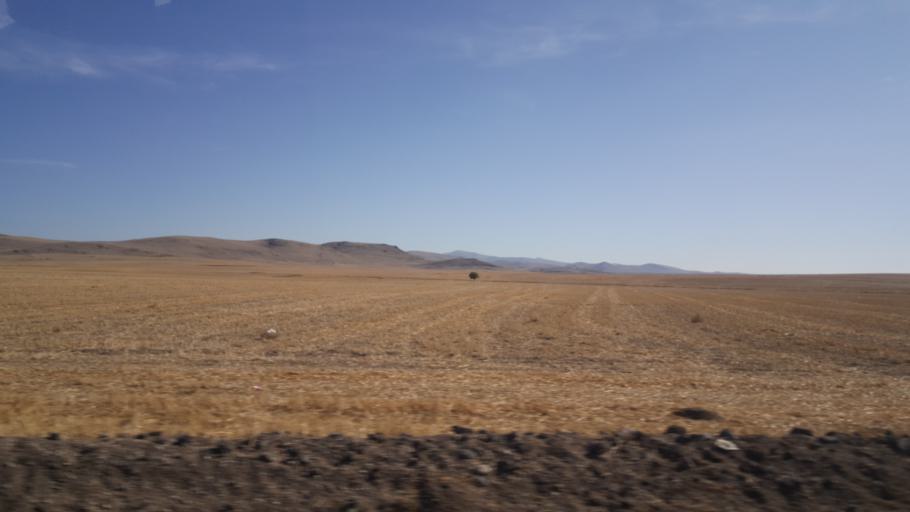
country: TR
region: Ankara
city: Yenice
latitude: 39.3500
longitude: 32.7707
